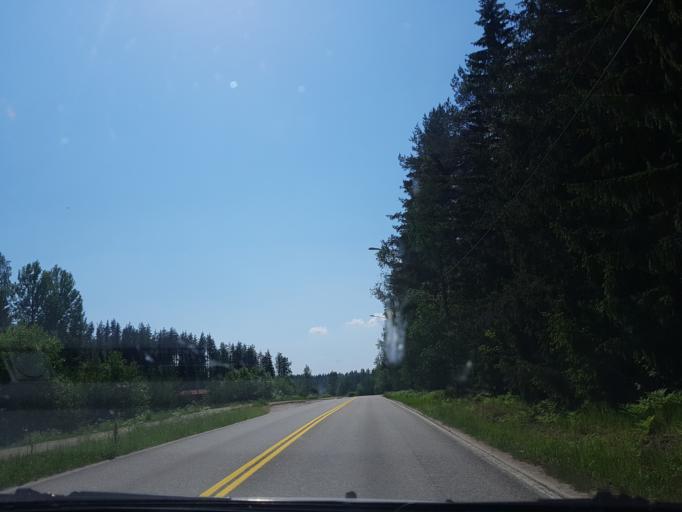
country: FI
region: Uusimaa
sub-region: Helsinki
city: Vihti
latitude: 60.3253
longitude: 24.4076
